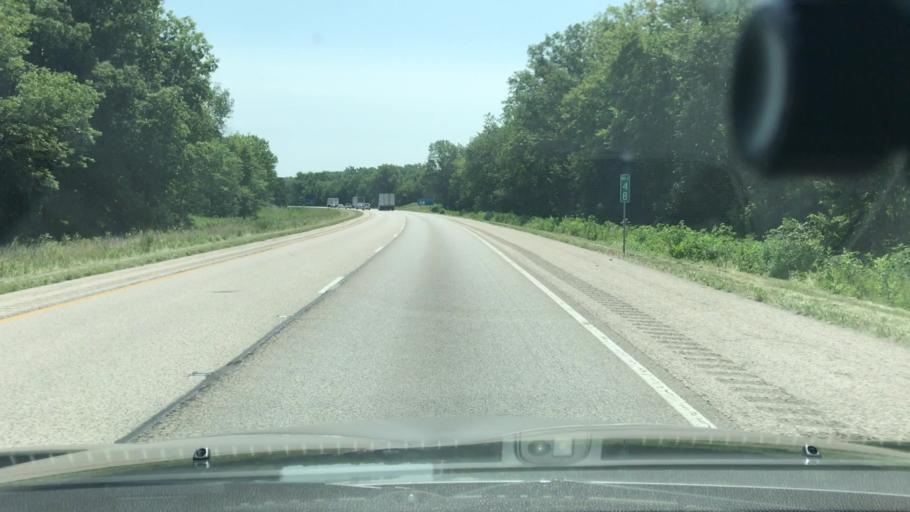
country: US
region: Illinois
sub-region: Washington County
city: Nashville
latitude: 38.4029
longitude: -89.4043
